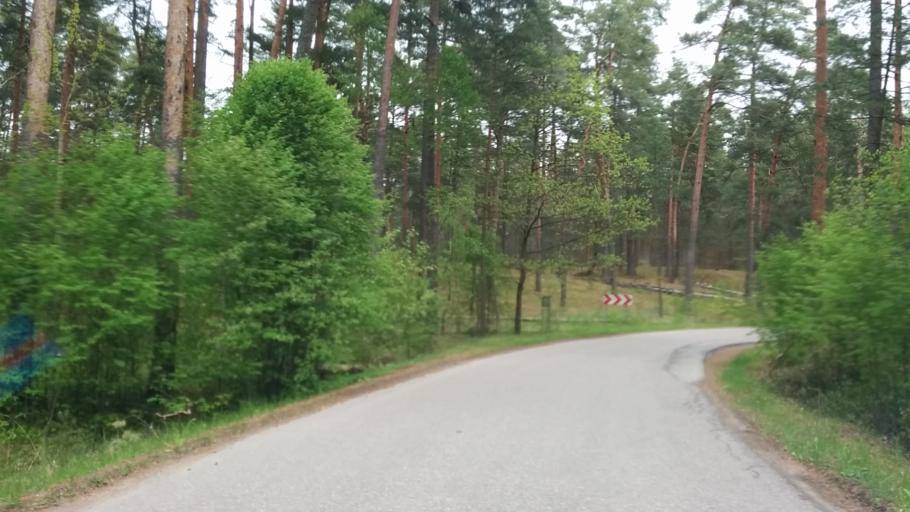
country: LV
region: Babite
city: Pinki
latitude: 56.9403
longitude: 23.9355
